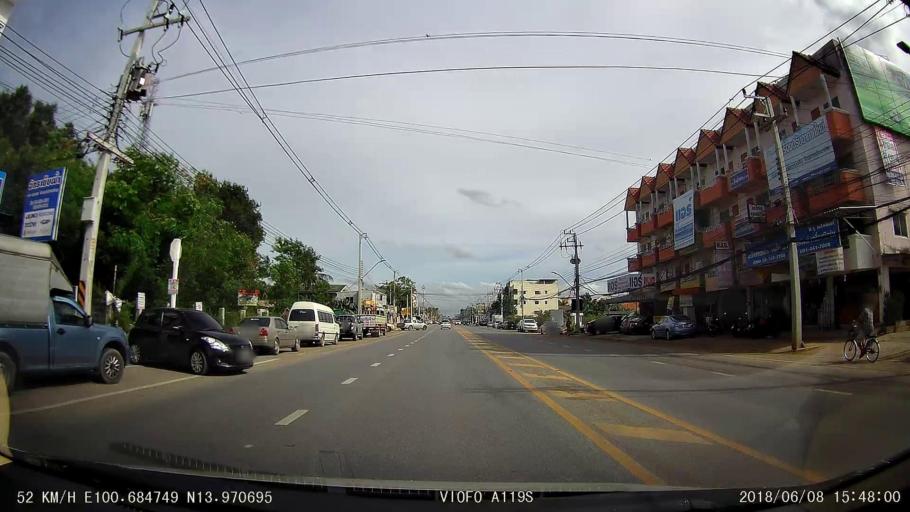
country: TH
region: Bangkok
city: Sai Mai
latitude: 13.9705
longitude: 100.6847
